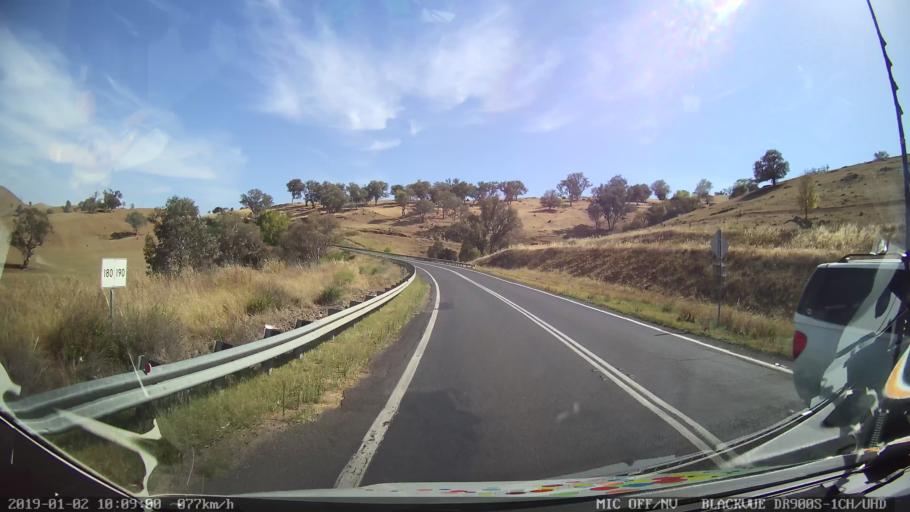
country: AU
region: New South Wales
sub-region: Gundagai
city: Gundagai
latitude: -35.1210
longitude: 148.1008
